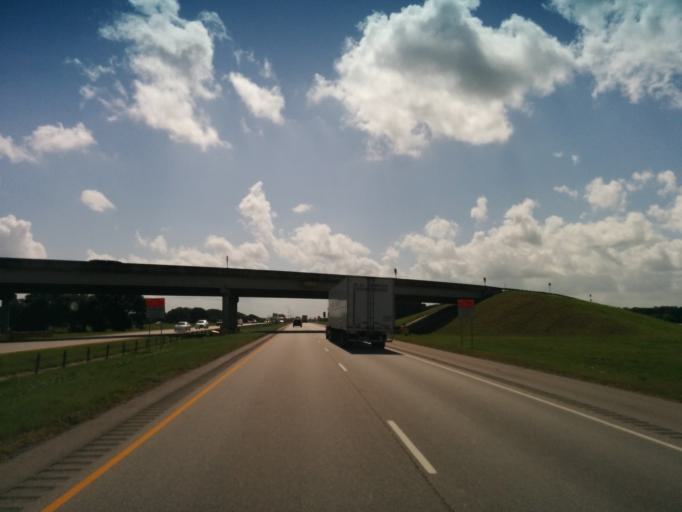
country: US
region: Texas
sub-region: Colorado County
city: Columbus
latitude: 29.6936
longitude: -96.5741
